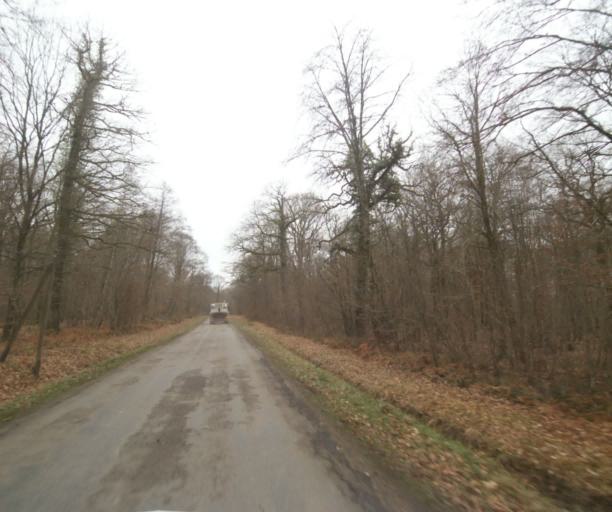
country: FR
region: Champagne-Ardenne
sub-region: Departement de la Haute-Marne
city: Wassy
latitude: 48.5252
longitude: 4.9759
